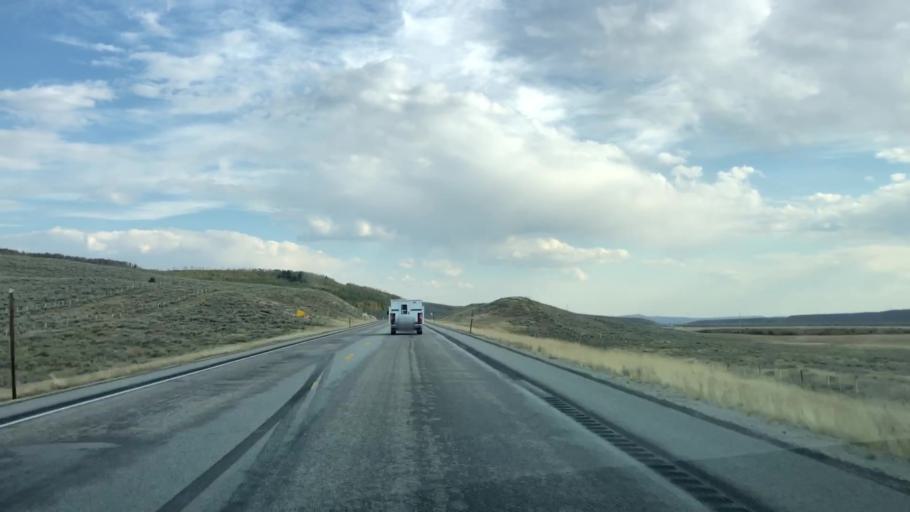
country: US
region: Wyoming
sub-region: Sublette County
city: Pinedale
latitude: 43.0942
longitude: -110.1664
